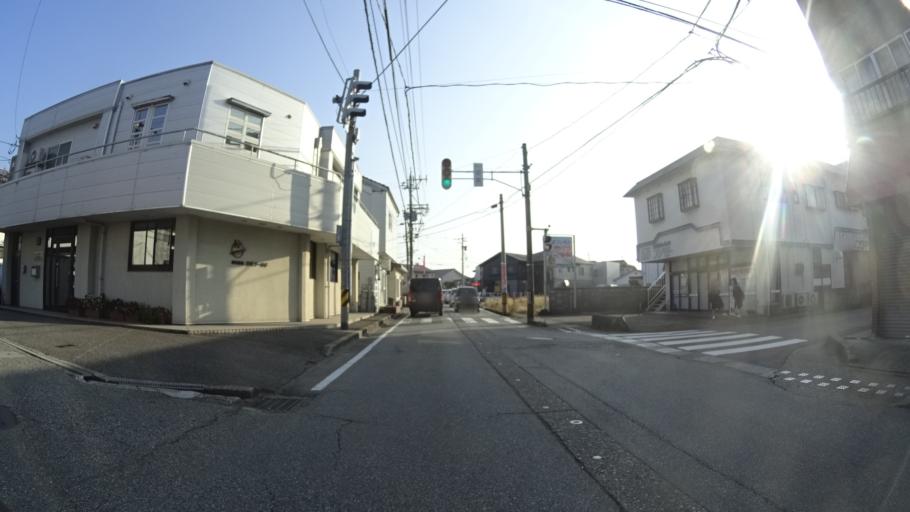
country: JP
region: Toyama
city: Toyama-shi
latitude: 36.6980
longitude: 137.2648
